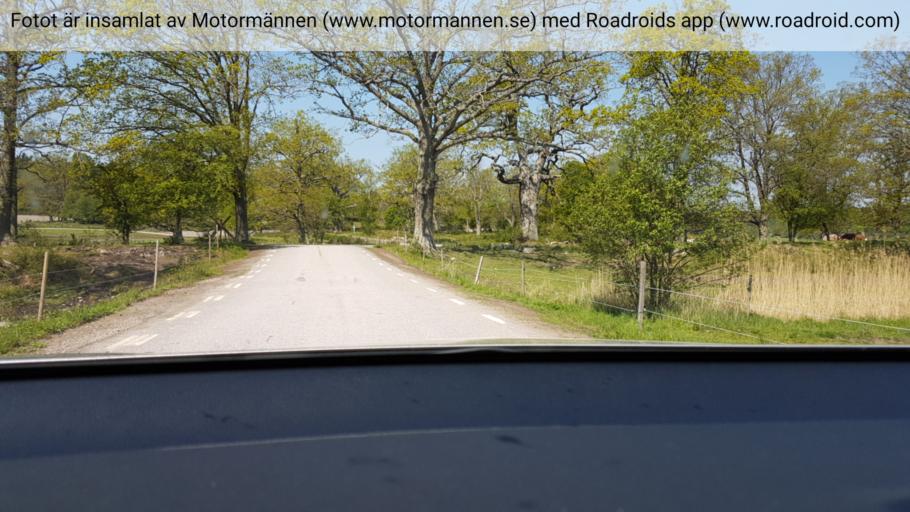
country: SE
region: Kalmar
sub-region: Vasterviks Kommun
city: Forserum
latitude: 57.8503
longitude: 16.5297
